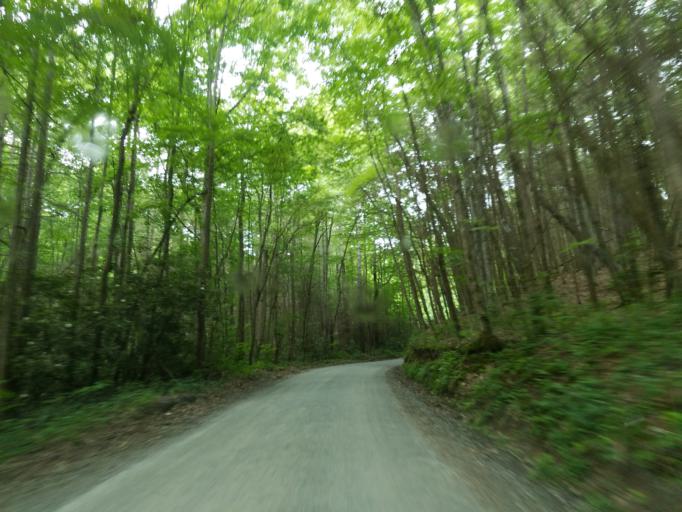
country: US
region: Georgia
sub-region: Fannin County
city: Blue Ridge
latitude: 34.7804
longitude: -84.3297
